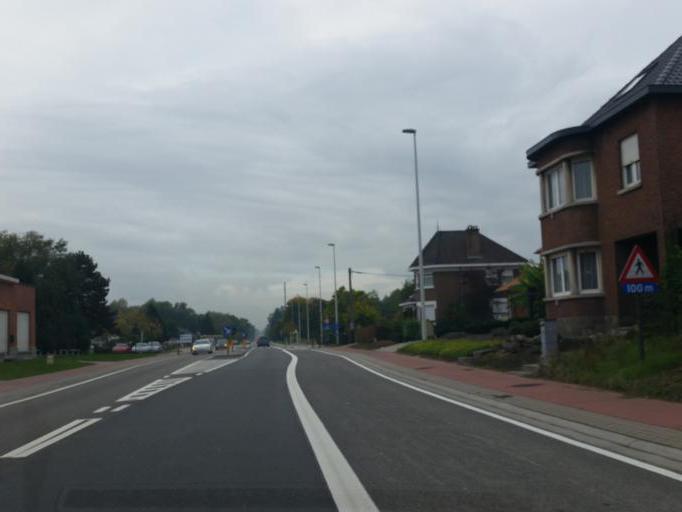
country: BE
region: Flanders
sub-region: Provincie Vlaams-Brabant
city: Steenokkerzeel
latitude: 50.9292
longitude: 4.5277
